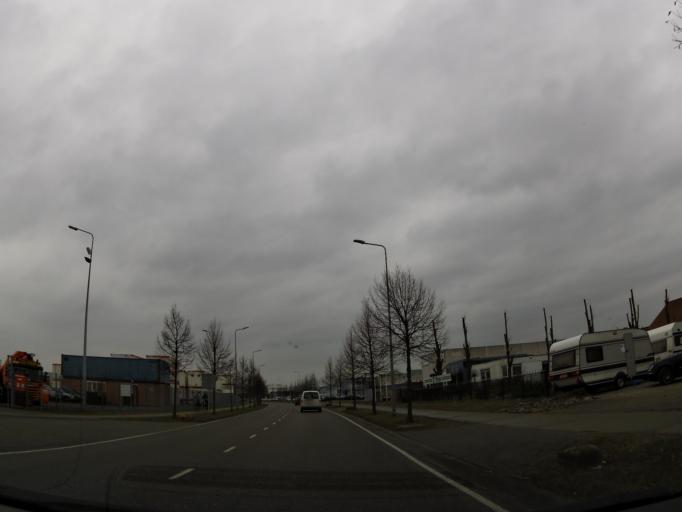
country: NL
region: Limburg
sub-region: Gemeente Sittard-Geleen
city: Sittard
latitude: 51.0132
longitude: 5.8741
